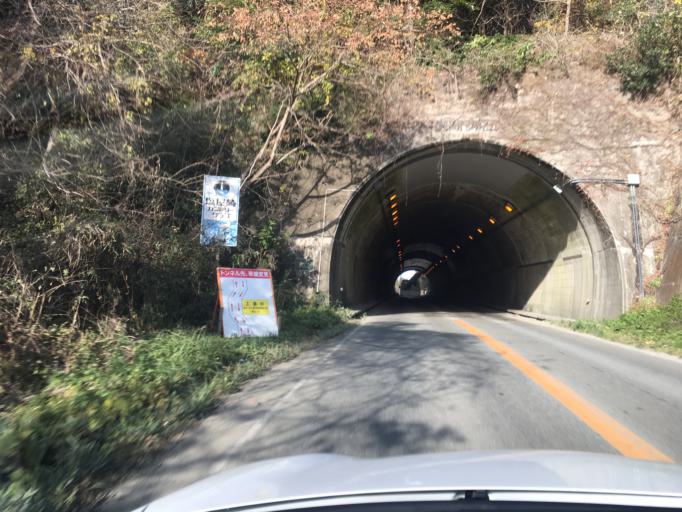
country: JP
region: Fukushima
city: Iwaki
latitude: 36.9975
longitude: 140.9666
